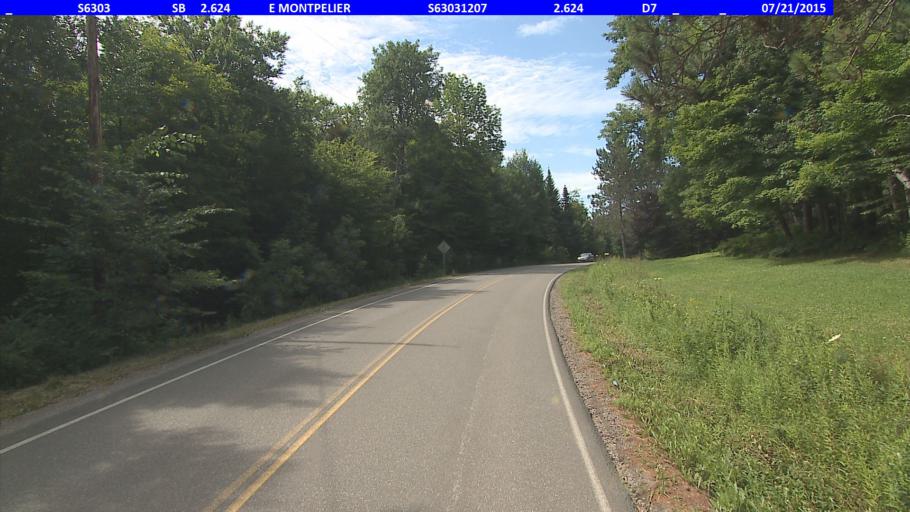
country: US
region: Vermont
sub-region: Washington County
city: Montpelier
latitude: 44.3051
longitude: -72.5303
